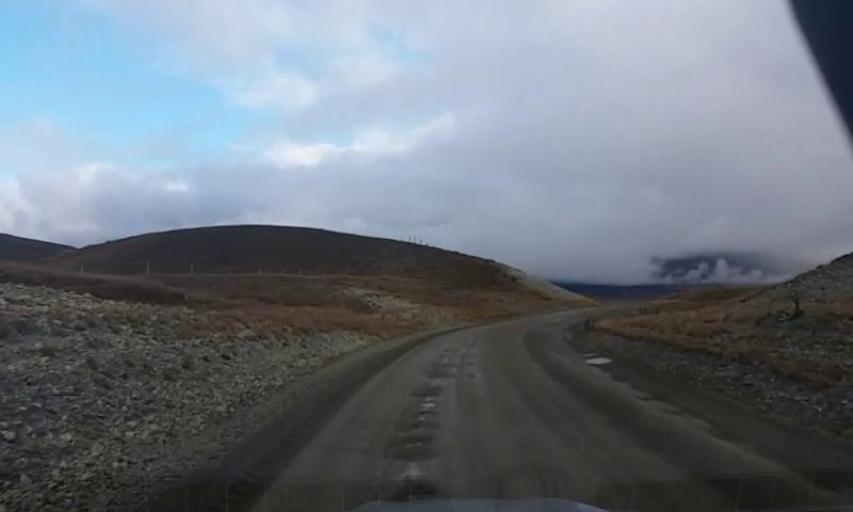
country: NZ
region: Canterbury
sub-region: Ashburton District
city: Methven
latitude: -43.6157
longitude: 171.1353
